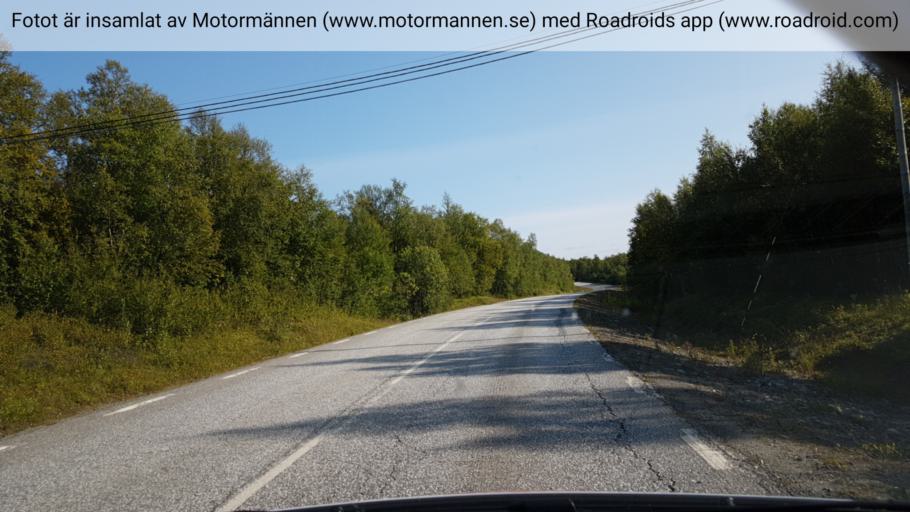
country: NO
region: Nordland
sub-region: Rana
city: Mo i Rana
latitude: 65.7795
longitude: 15.1304
